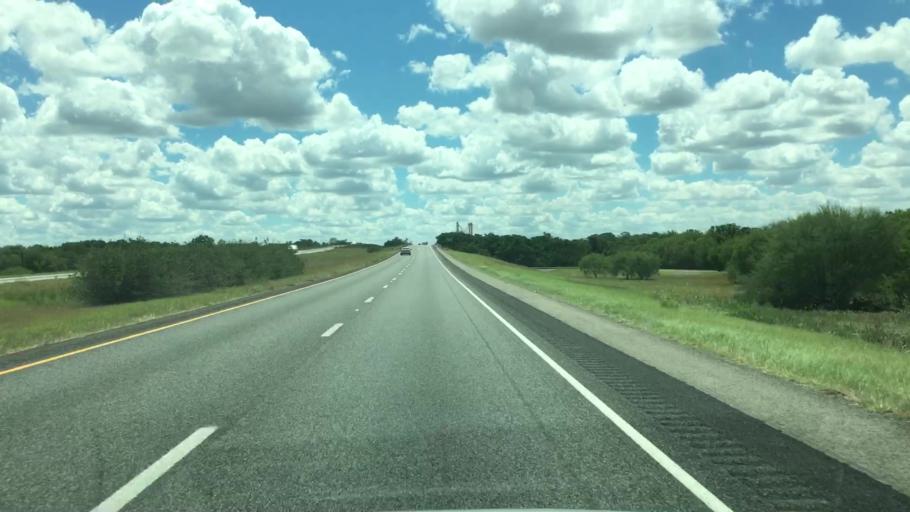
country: US
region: Texas
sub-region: Atascosa County
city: Pleasanton
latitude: 28.9660
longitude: -98.4366
